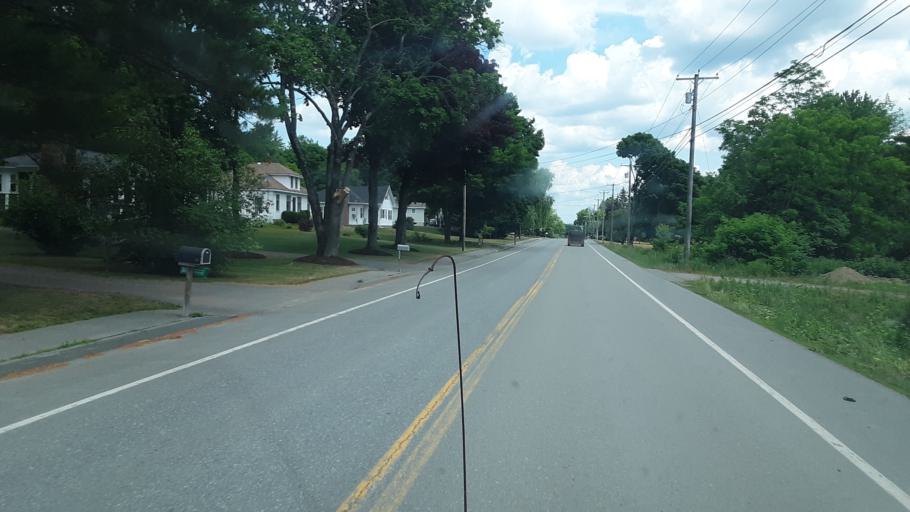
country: US
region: Maine
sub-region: Penobscot County
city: Hampden
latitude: 44.7632
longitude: -68.8060
